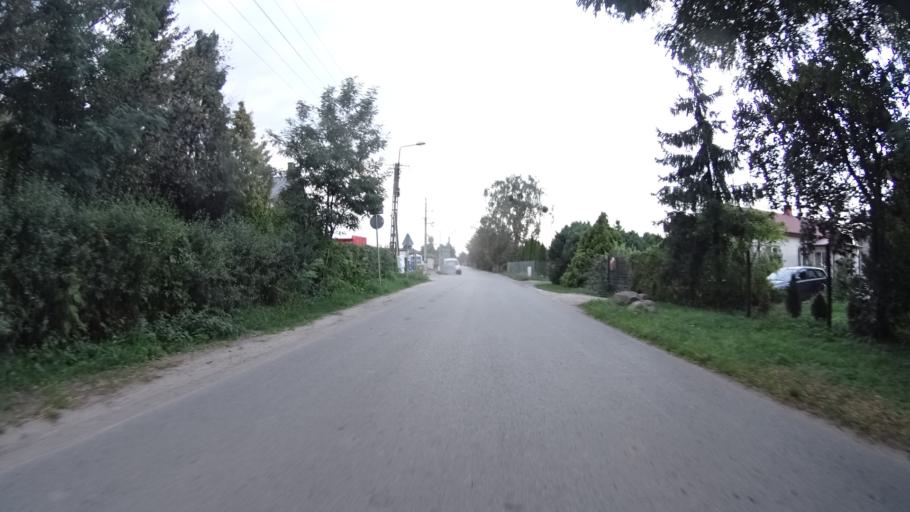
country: PL
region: Masovian Voivodeship
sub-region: Powiat warszawski zachodni
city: Stare Babice
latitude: 52.2371
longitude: 20.8270
